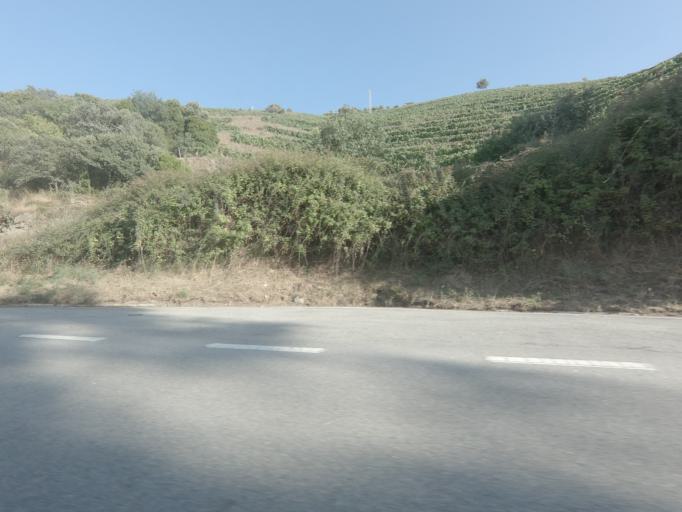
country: PT
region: Viseu
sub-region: Tabuaco
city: Tabuaco
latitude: 41.1547
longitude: -7.5913
